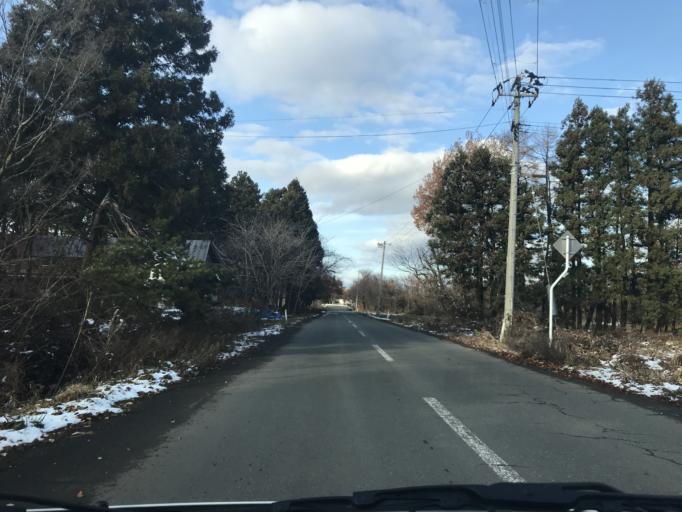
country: JP
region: Iwate
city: Kitakami
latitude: 39.2526
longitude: 141.0324
